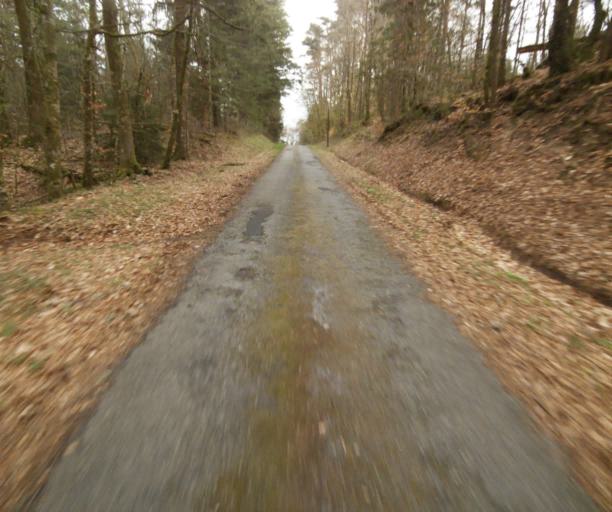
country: FR
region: Limousin
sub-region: Departement de la Correze
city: Argentat
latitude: 45.2227
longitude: 1.9643
